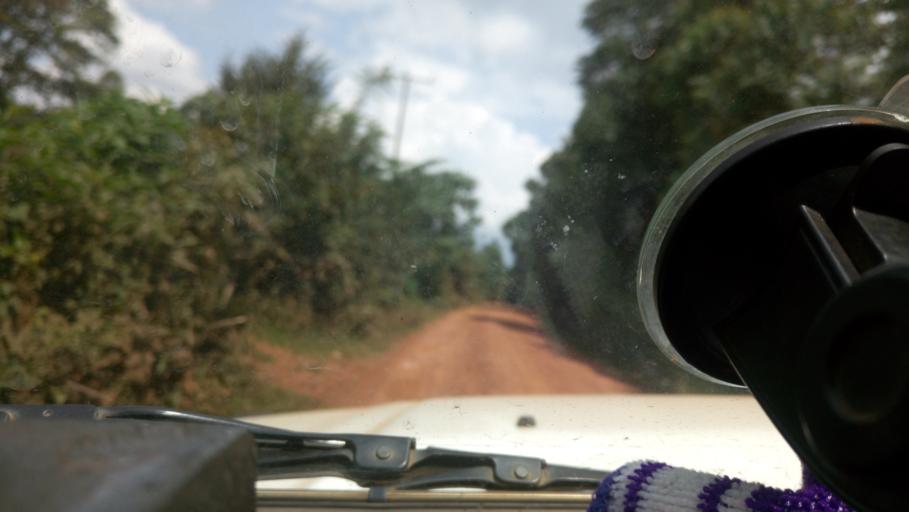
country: KE
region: Kericho
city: Litein
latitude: -0.6040
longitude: 35.1799
